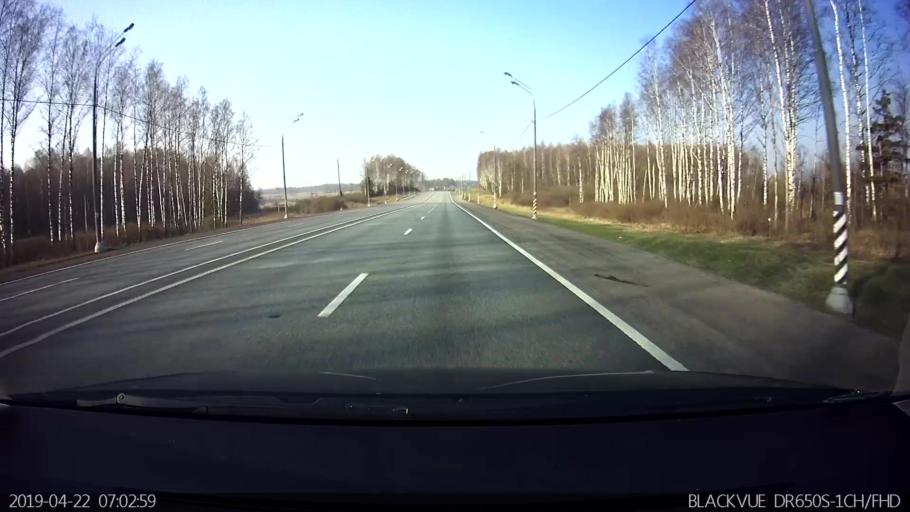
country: RU
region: Smolensk
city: Gagarin
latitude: 55.3860
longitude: 34.7083
